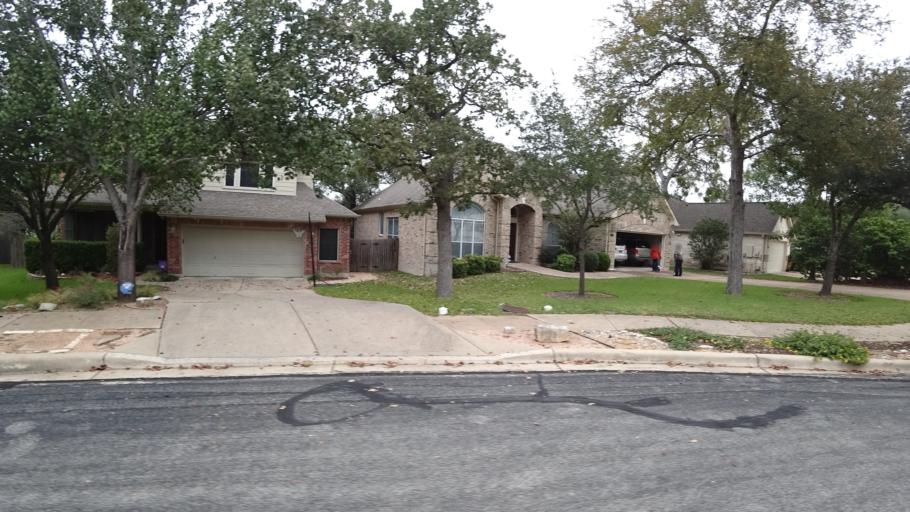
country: US
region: Texas
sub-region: Travis County
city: Shady Hollow
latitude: 30.1898
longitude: -97.8987
